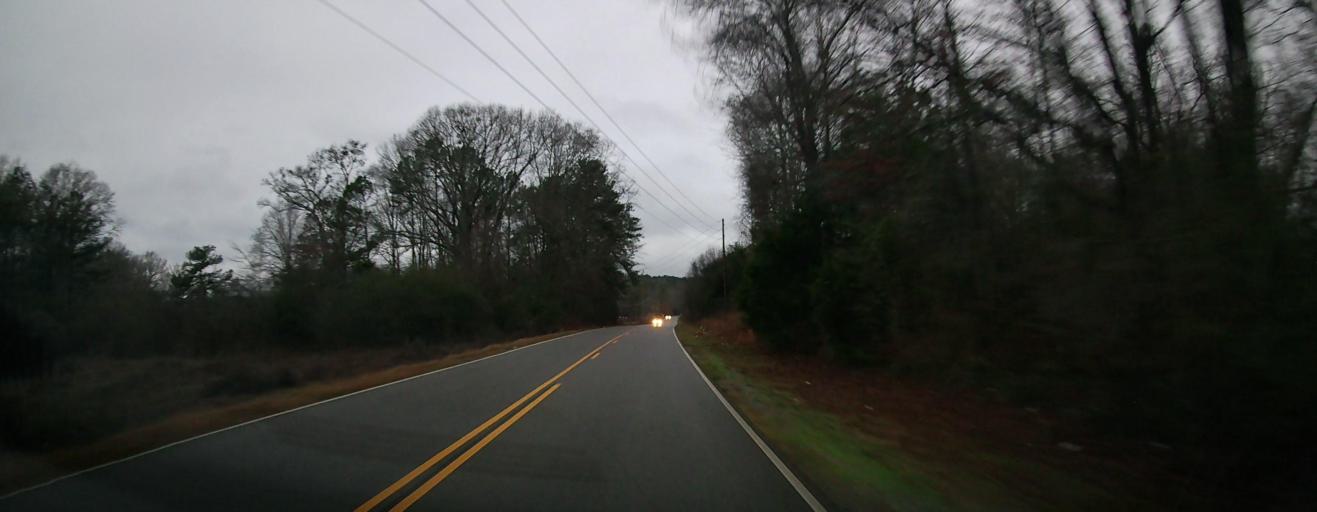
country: US
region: Alabama
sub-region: Tuscaloosa County
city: Vance
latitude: 33.1210
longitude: -87.2250
